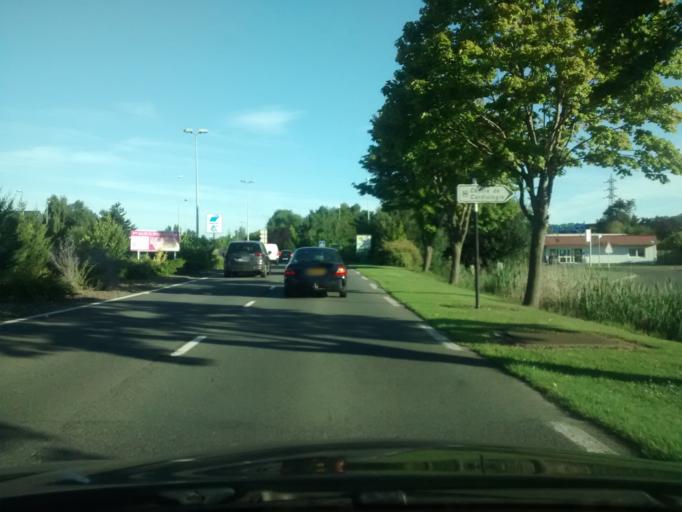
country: FR
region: Lower Normandy
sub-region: Departement du Calvados
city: Touques
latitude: 49.3462
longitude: 0.0982
